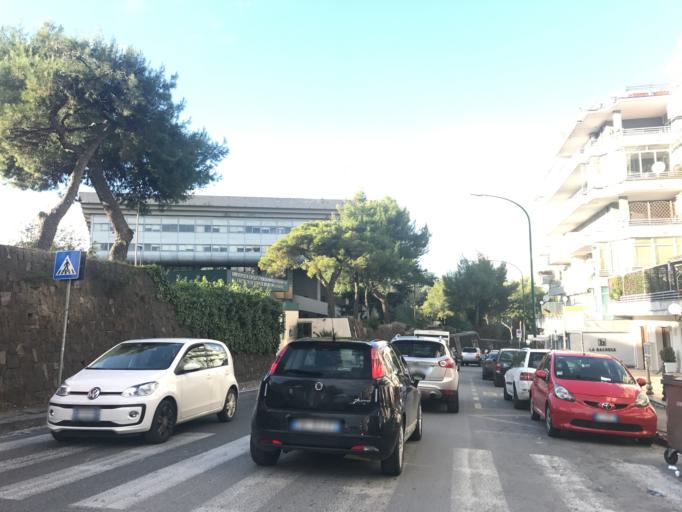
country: IT
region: Campania
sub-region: Provincia di Napoli
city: Napoli
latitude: 40.8691
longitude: 14.2226
